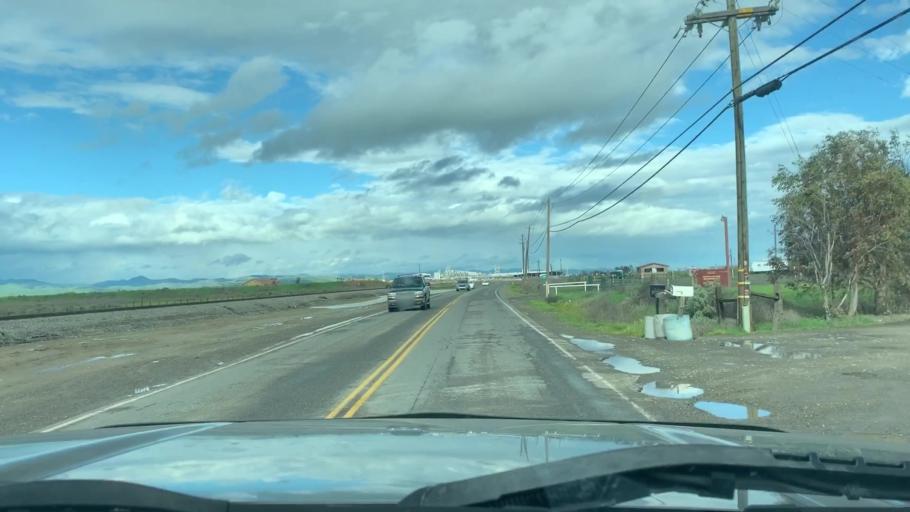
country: US
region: California
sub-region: Merced County
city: Los Banos
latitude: 37.1033
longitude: -120.9342
